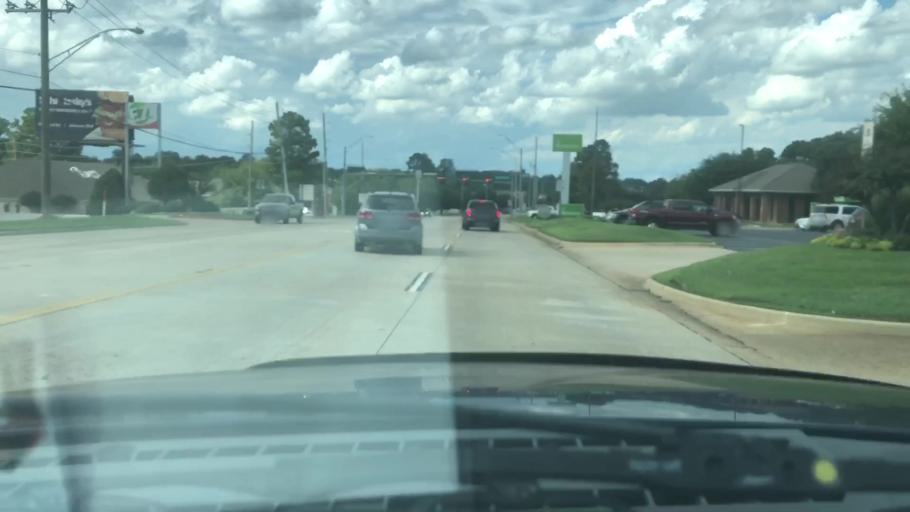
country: US
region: Arkansas
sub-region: Miller County
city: Texarkana
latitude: 33.4679
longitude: -94.0676
